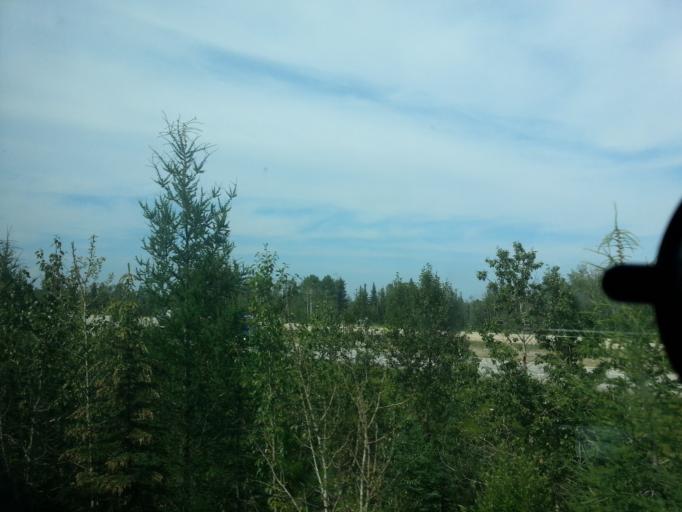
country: CA
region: Alberta
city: Hinton
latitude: 53.5514
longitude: -117.1539
